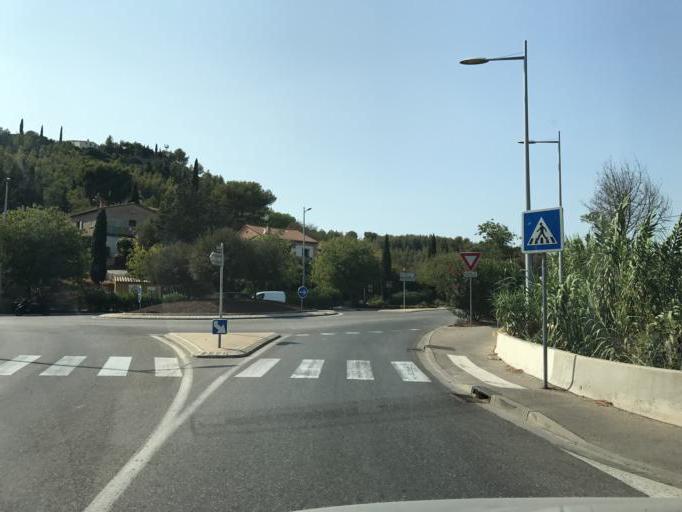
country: FR
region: Provence-Alpes-Cote d'Azur
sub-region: Departement du Var
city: Bandol
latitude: 43.1452
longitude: 5.7685
